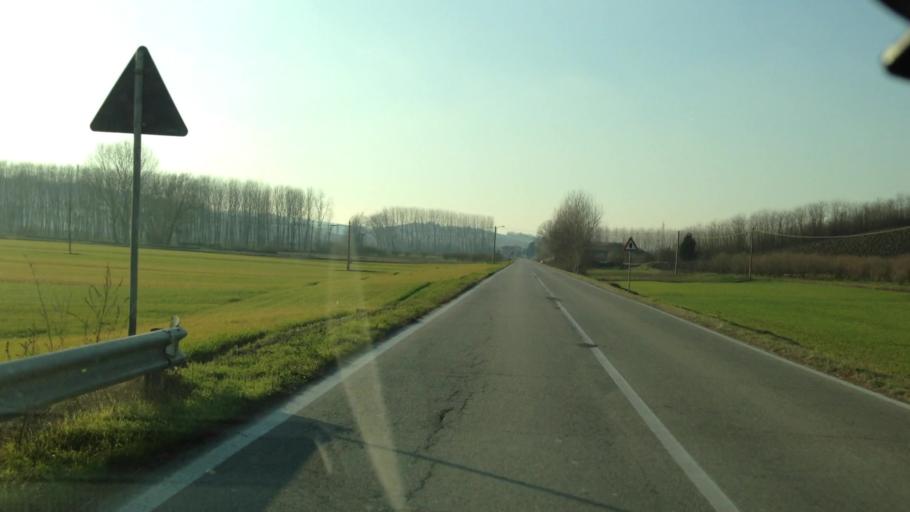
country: IT
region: Piedmont
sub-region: Provincia di Asti
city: Montaldo Scarampi
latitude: 44.8169
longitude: 8.2671
